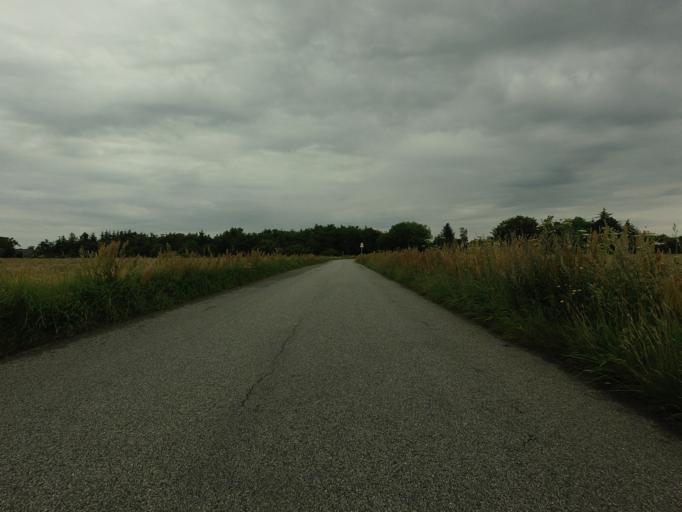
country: DK
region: North Denmark
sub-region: Alborg Kommune
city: Vadum
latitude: 57.1113
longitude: 9.8816
